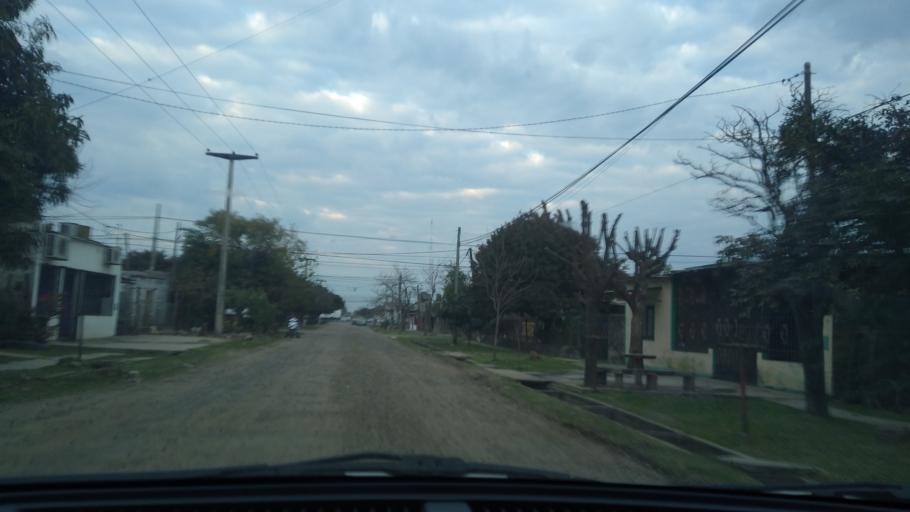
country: AR
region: Chaco
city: Resistencia
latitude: -27.4798
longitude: -58.9661
